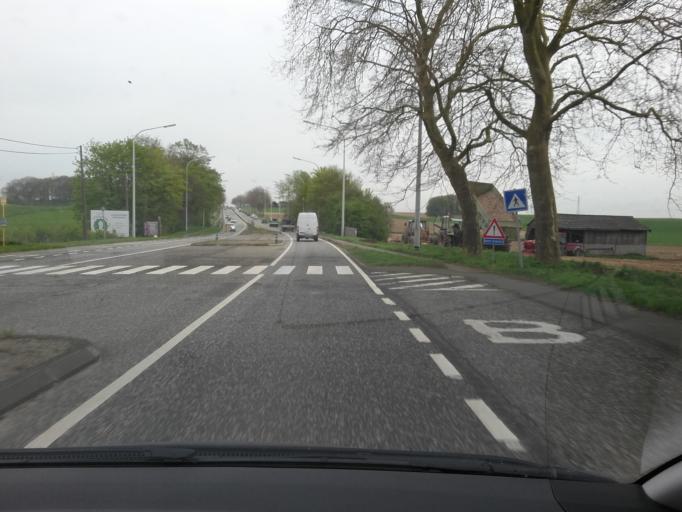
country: BE
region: Wallonia
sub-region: Province du Brabant Wallon
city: Genappe
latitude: 50.6400
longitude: 4.4230
